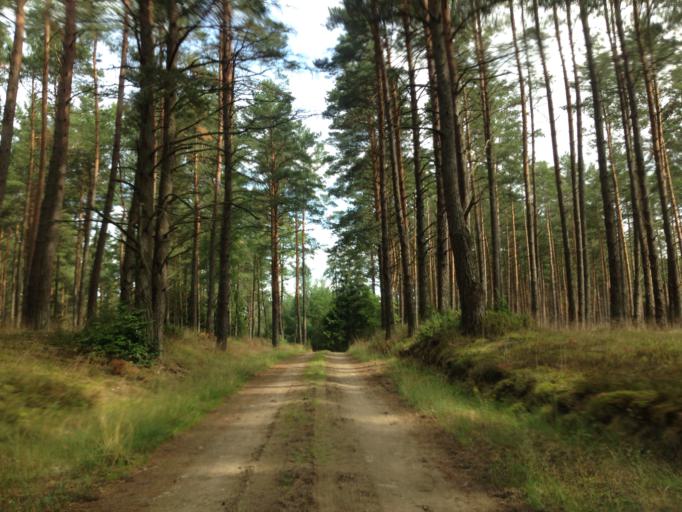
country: PL
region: Pomeranian Voivodeship
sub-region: Powiat bytowski
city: Studzienice
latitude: 54.0473
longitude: 17.6481
